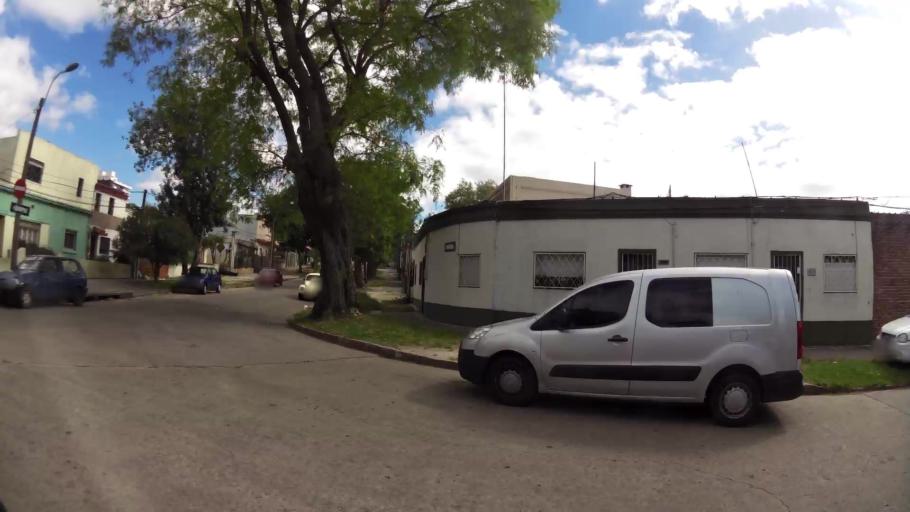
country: UY
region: Montevideo
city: Montevideo
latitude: -34.8888
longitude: -56.1315
